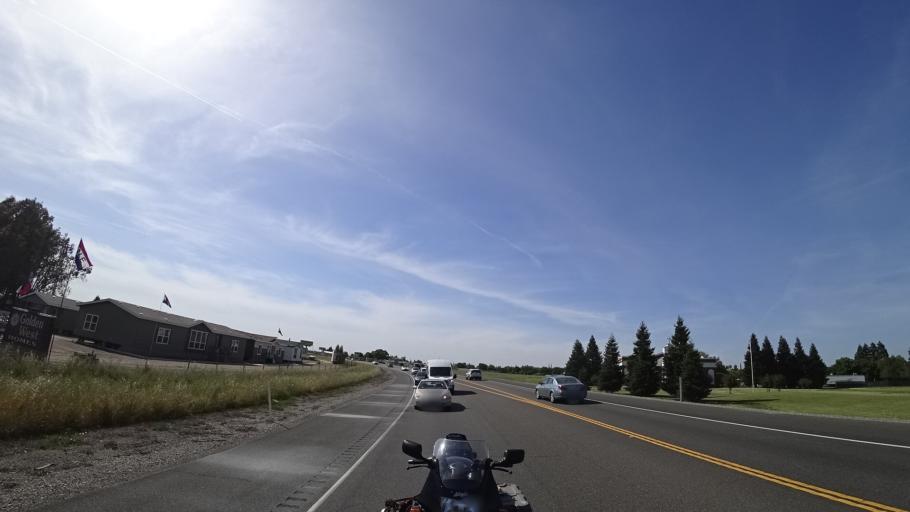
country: US
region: California
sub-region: Butte County
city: Chico
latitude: 39.7910
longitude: -121.8922
